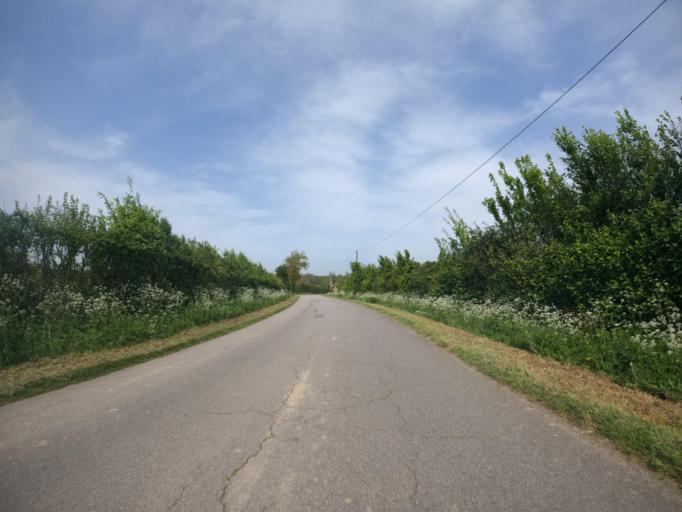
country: FR
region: Poitou-Charentes
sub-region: Departement des Deux-Sevres
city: La Chapelle-Saint-Laurent
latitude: 46.7092
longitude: -0.5074
